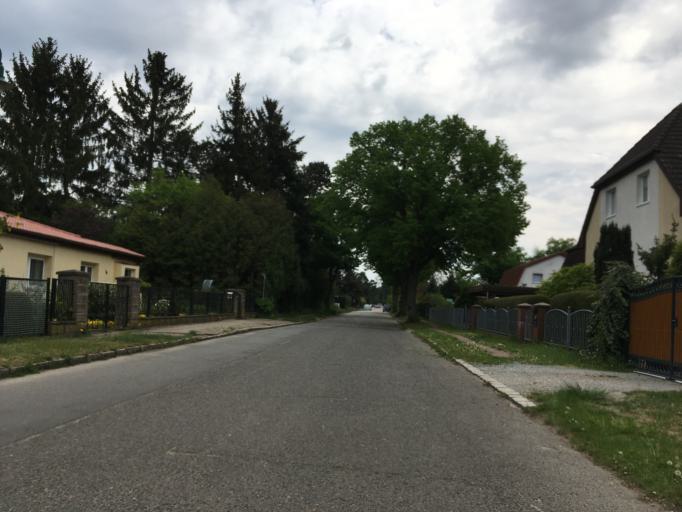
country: DE
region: Berlin
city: Buch
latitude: 52.6425
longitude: 13.5294
